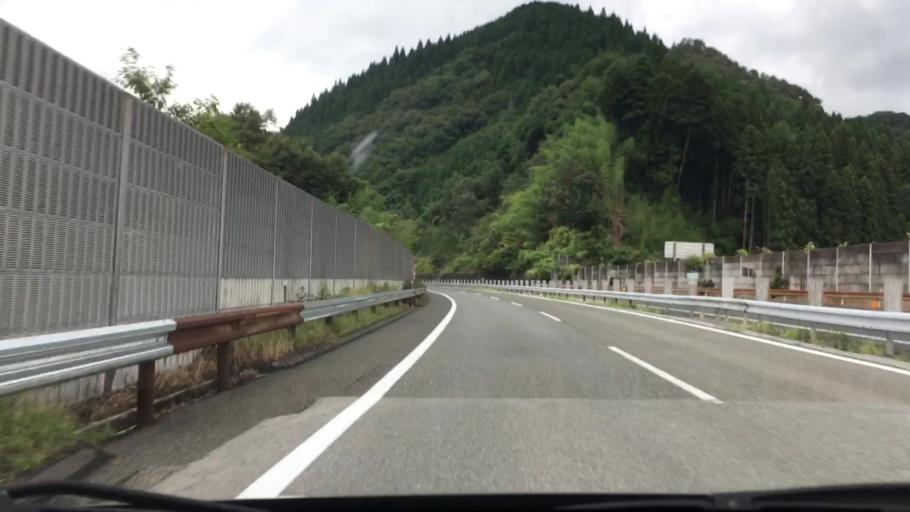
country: JP
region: Okayama
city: Niimi
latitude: 35.0131
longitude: 133.4335
